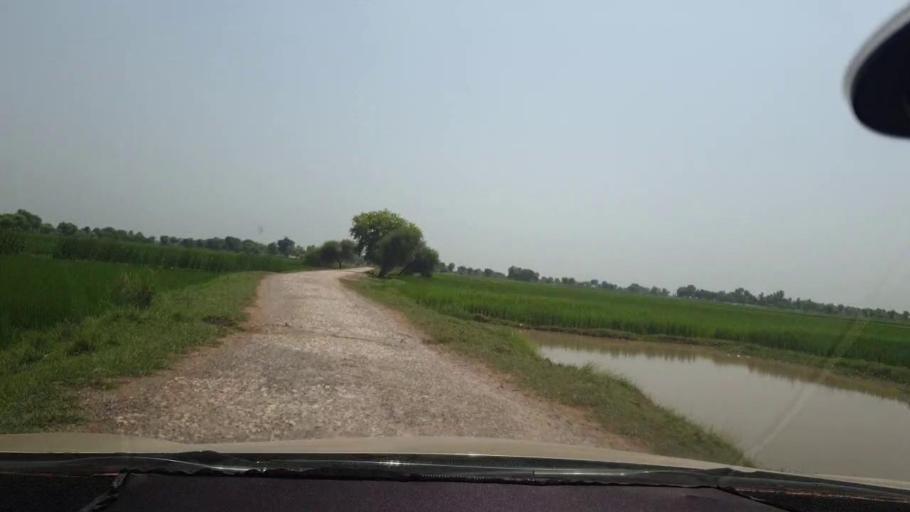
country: PK
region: Sindh
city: Kambar
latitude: 27.6428
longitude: 67.9322
